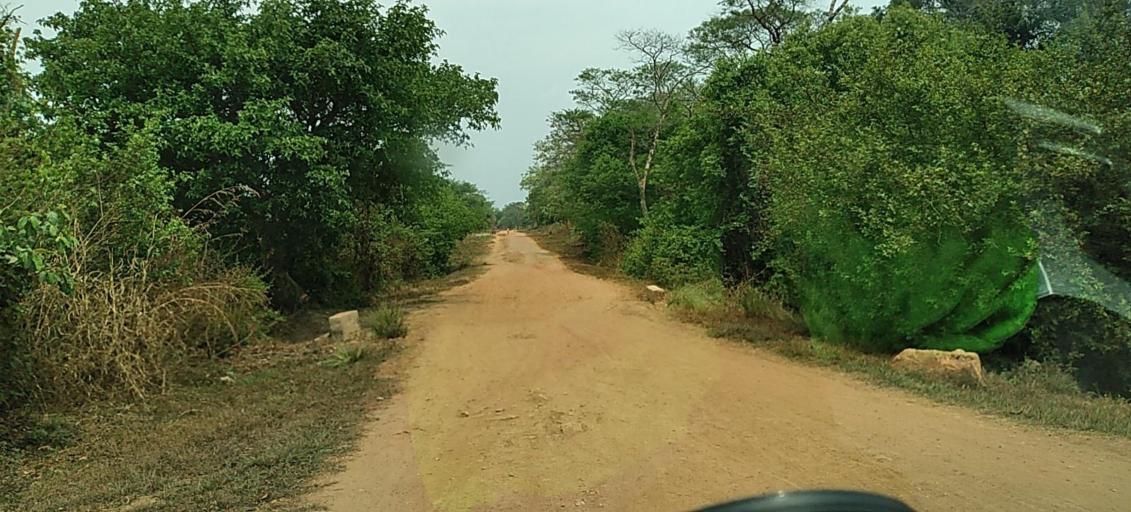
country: ZM
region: North-Western
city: Solwezi
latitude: -12.7966
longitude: 26.5332
